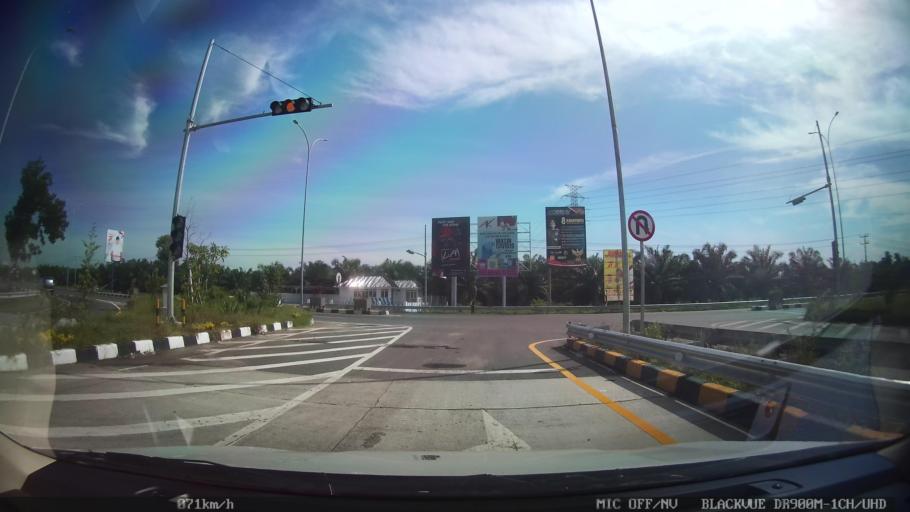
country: ID
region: North Sumatra
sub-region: Kabupaten Langkat
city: Stabat
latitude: 3.7328
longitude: 98.4911
